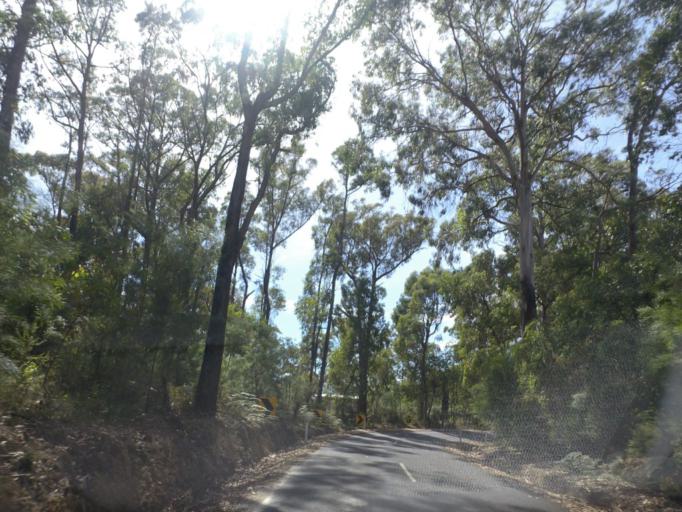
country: AU
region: Victoria
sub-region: Nillumbik
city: Saint Andrews
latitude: -37.5074
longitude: 145.3733
